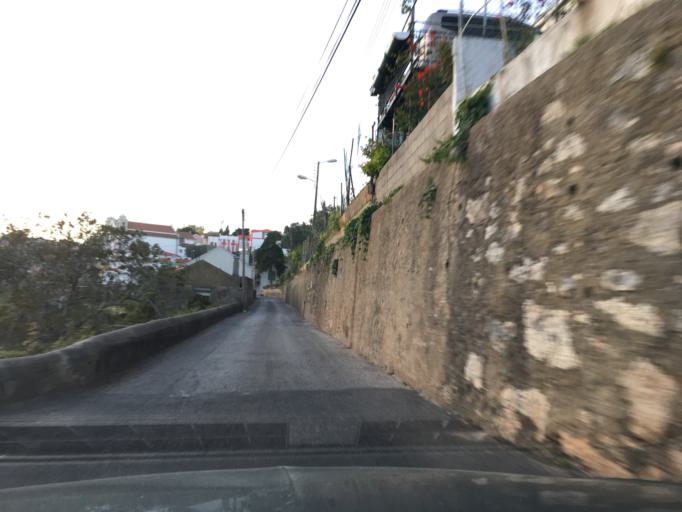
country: PT
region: Lisbon
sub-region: Oeiras
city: Barcarena
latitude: 38.7293
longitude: -9.2769
